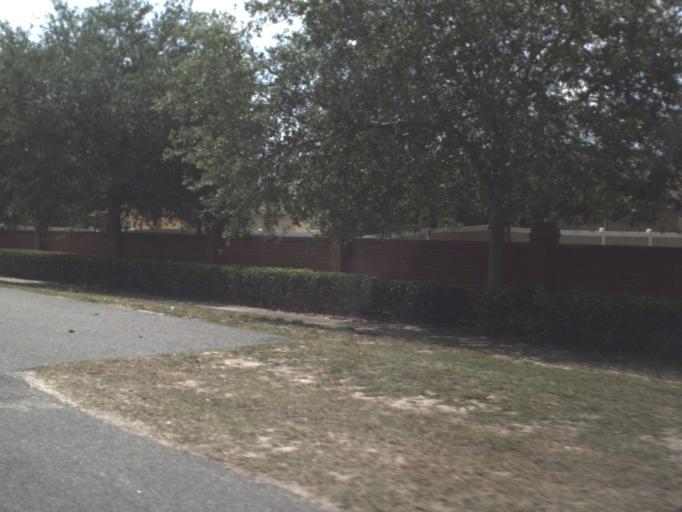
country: US
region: Florida
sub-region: Lake County
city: Howie In The Hills
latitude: 28.7561
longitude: -81.7638
